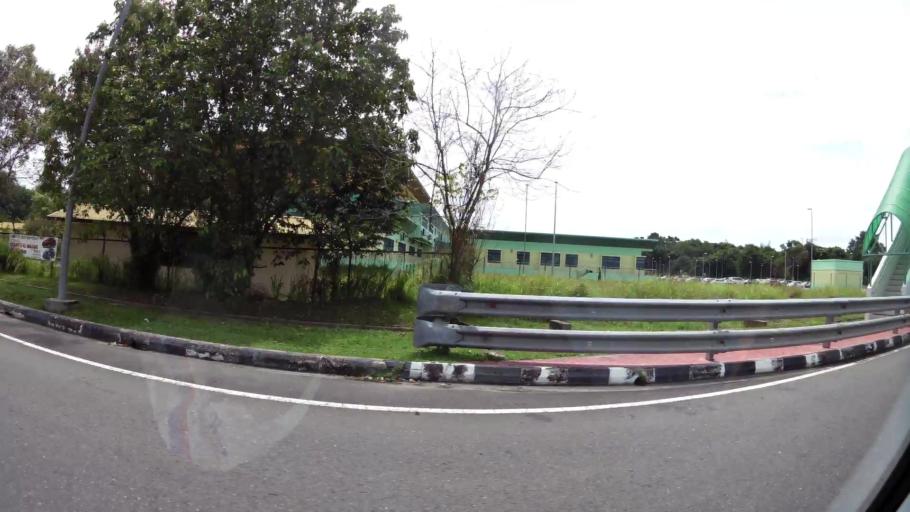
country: BN
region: Brunei and Muara
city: Bandar Seri Begawan
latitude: 4.9444
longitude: 114.9411
